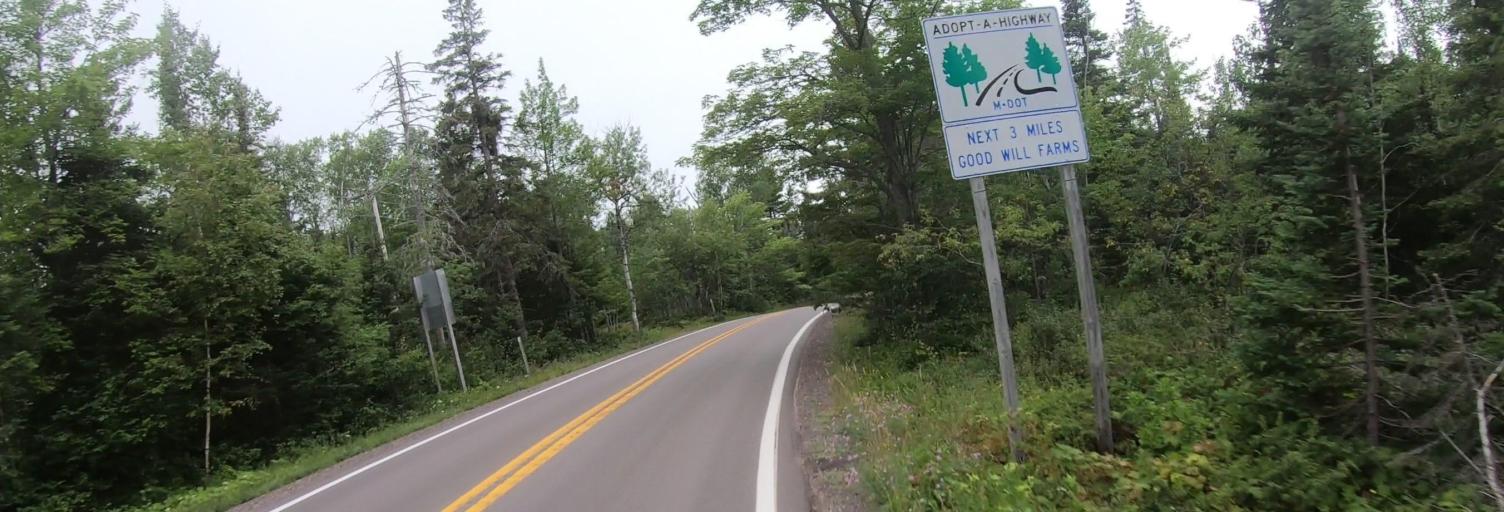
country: US
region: Michigan
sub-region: Keweenaw County
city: Eagle River
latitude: 47.4789
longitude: -87.9390
